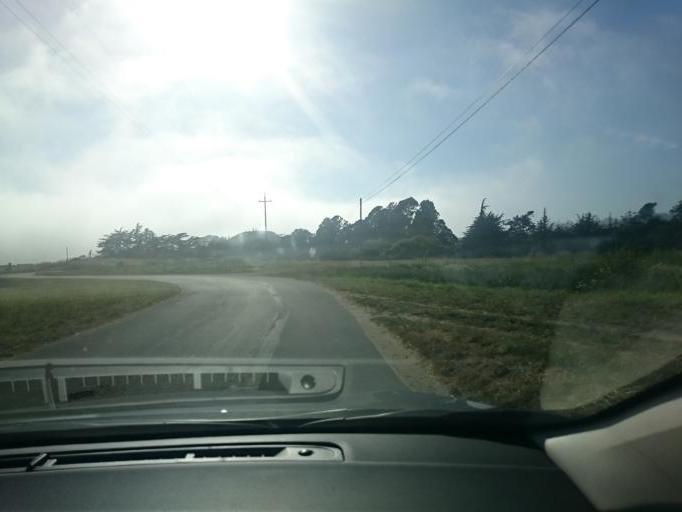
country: US
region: California
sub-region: Santa Cruz County
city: Santa Cruz
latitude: 36.9610
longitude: -122.0871
